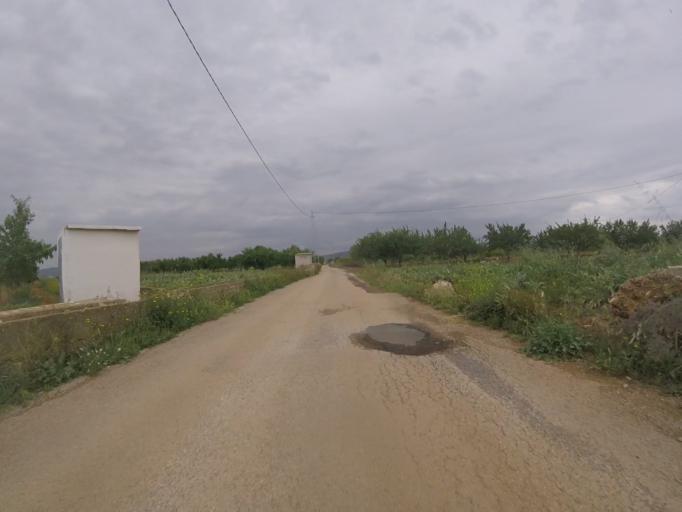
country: ES
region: Valencia
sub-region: Provincia de Castello
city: Torreblanca
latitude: 40.2174
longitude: 0.2265
